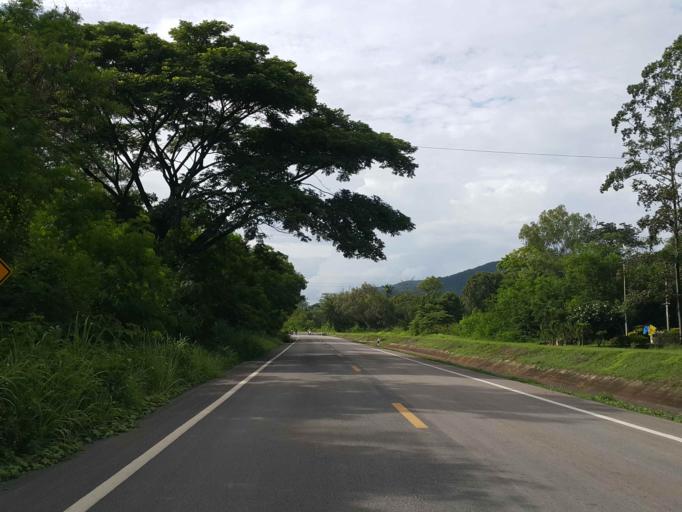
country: TH
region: Chiang Mai
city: San Sai
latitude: 18.9151
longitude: 99.1486
